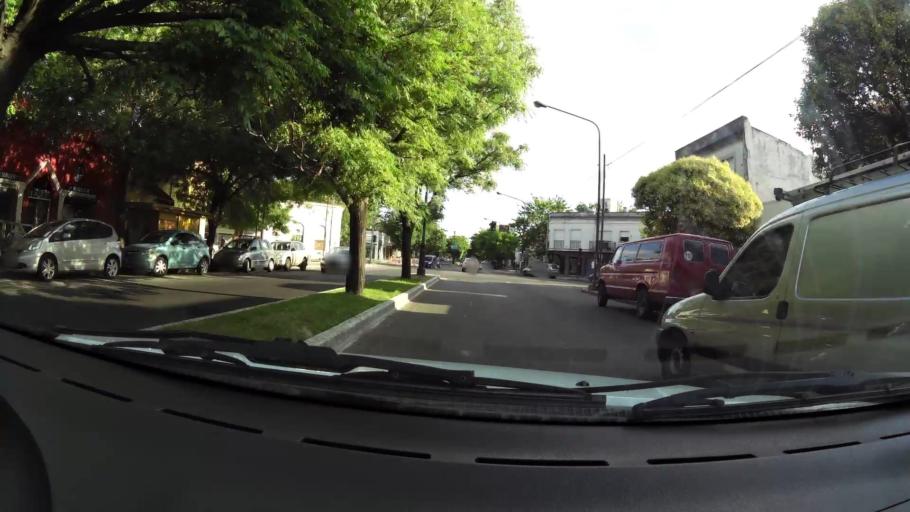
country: AR
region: Buenos Aires
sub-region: Partido de La Plata
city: La Plata
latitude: -34.9013
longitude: -57.9559
